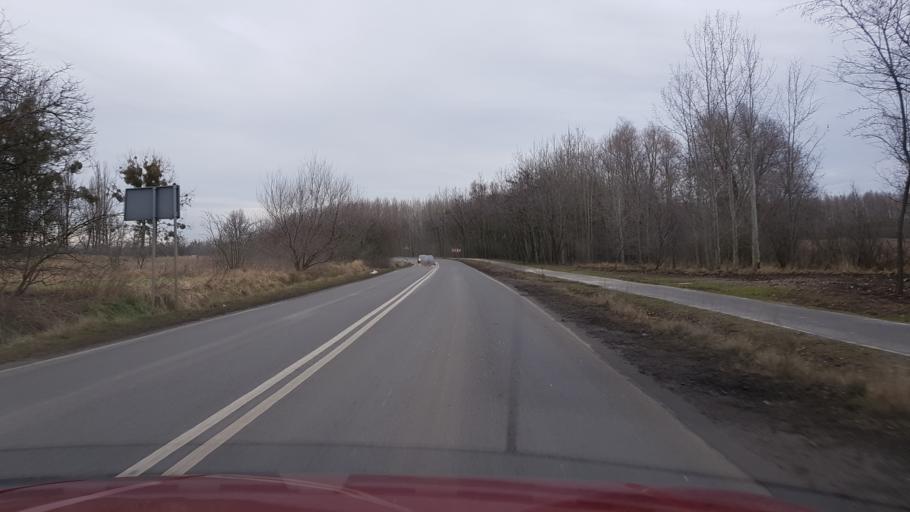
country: PL
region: West Pomeranian Voivodeship
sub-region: Powiat policki
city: Police
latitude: 53.5844
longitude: 14.5517
